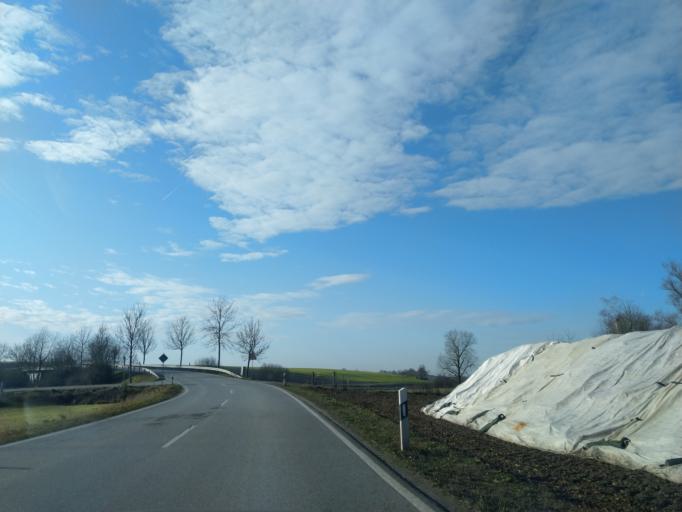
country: DE
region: Bavaria
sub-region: Lower Bavaria
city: Moos
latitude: 48.7384
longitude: 12.9426
